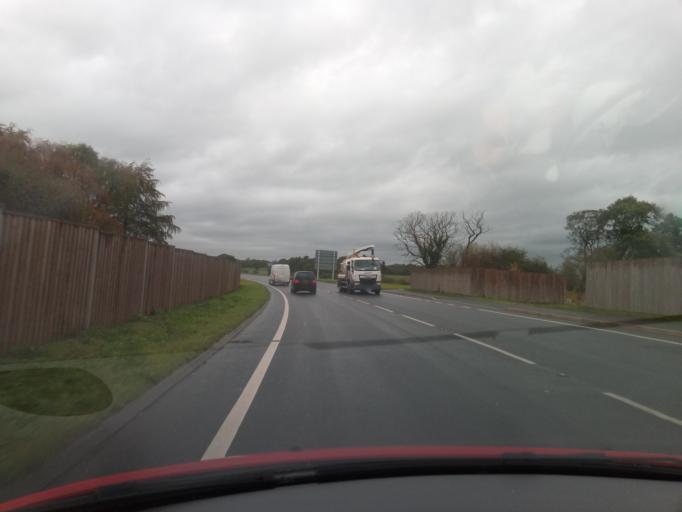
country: GB
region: England
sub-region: Lancashire
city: Preston
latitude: 53.8125
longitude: -2.7194
